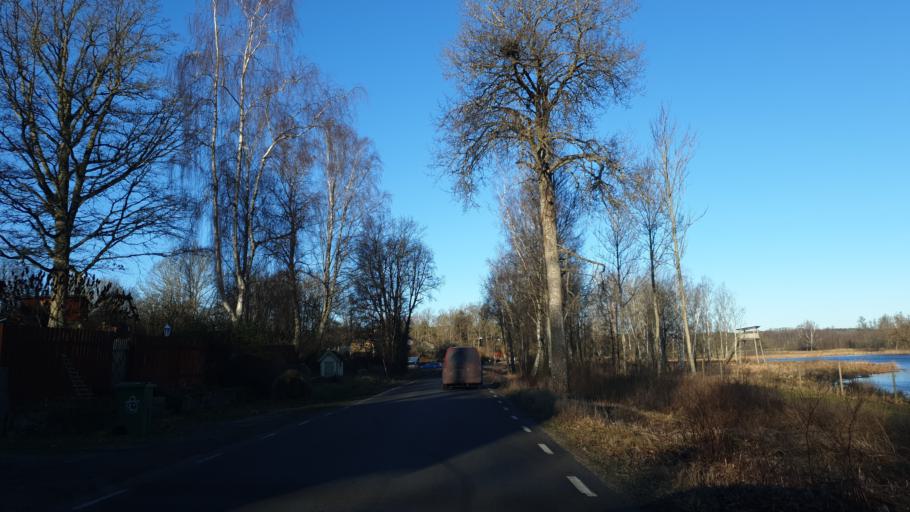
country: SE
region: Blekinge
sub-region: Karlskrona Kommun
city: Nattraby
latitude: 56.2623
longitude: 15.5099
